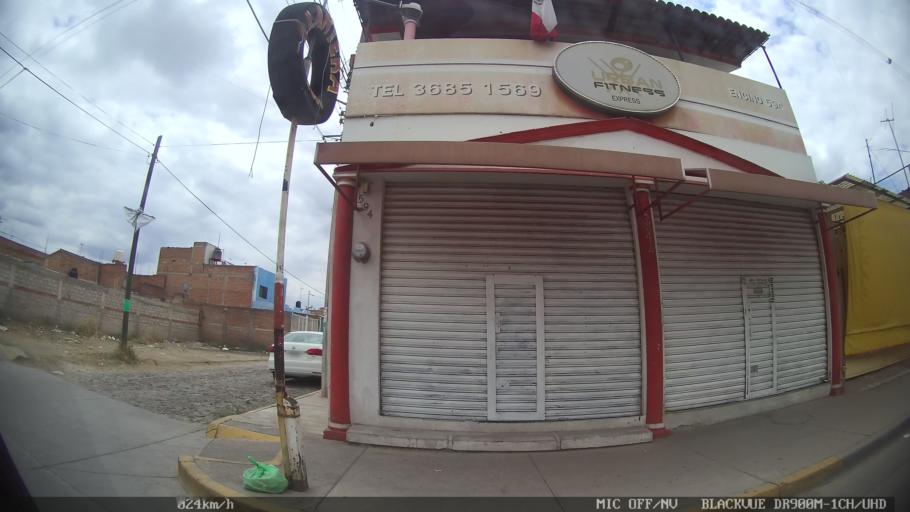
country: MX
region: Jalisco
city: Tonala
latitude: 20.6459
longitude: -103.2535
